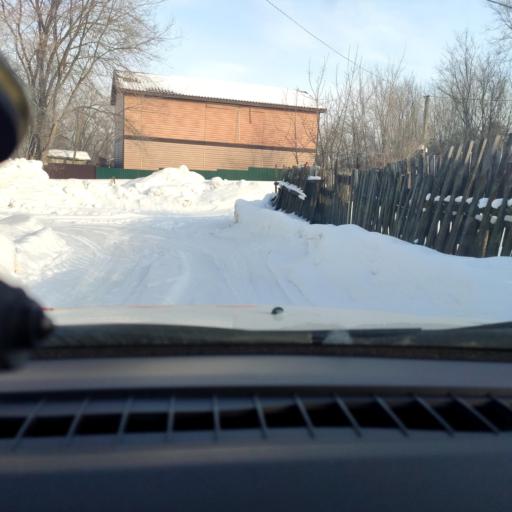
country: RU
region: Samara
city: Samara
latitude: 53.1295
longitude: 50.2594
